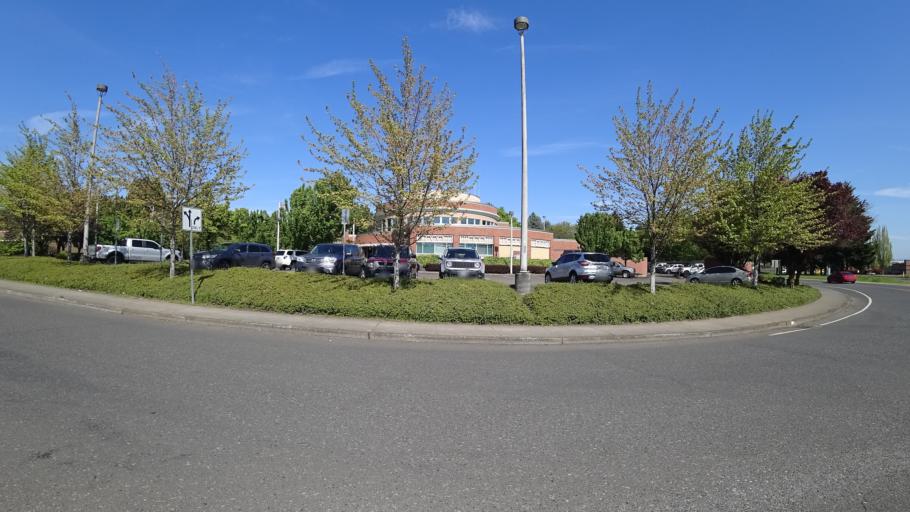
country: US
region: Oregon
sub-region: Clackamas County
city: Milwaukie
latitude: 45.4460
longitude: -122.6297
